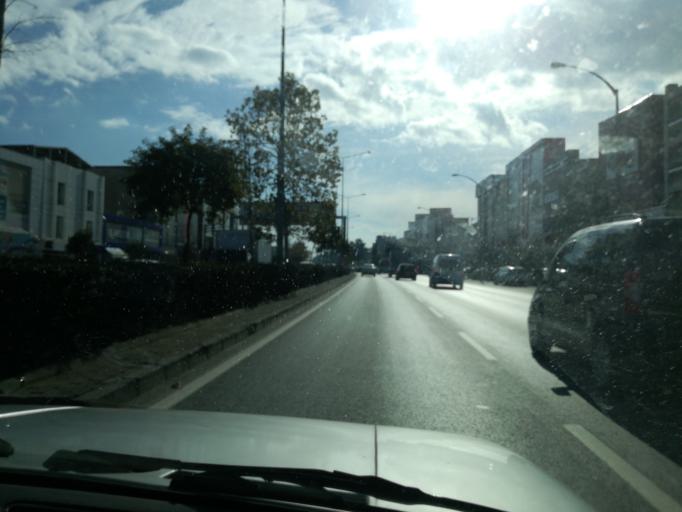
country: TR
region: Izmir
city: Karabaglar
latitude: 38.3742
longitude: 27.1350
